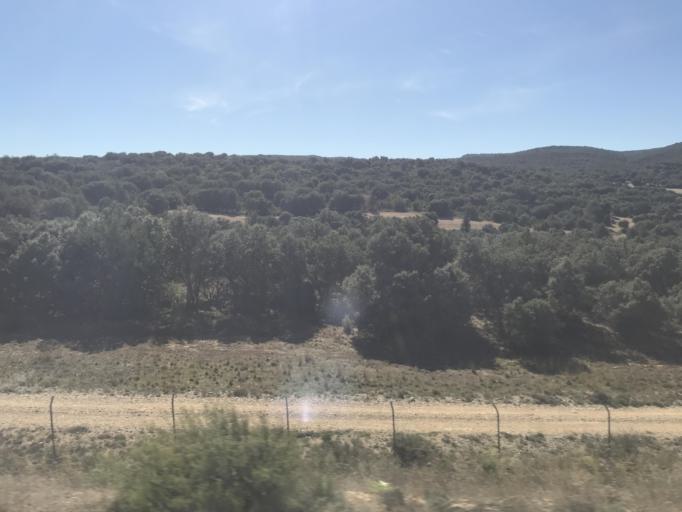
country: ES
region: Castille and Leon
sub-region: Provincia de Soria
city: Arcos de Jalon
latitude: 41.1771
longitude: -2.2334
